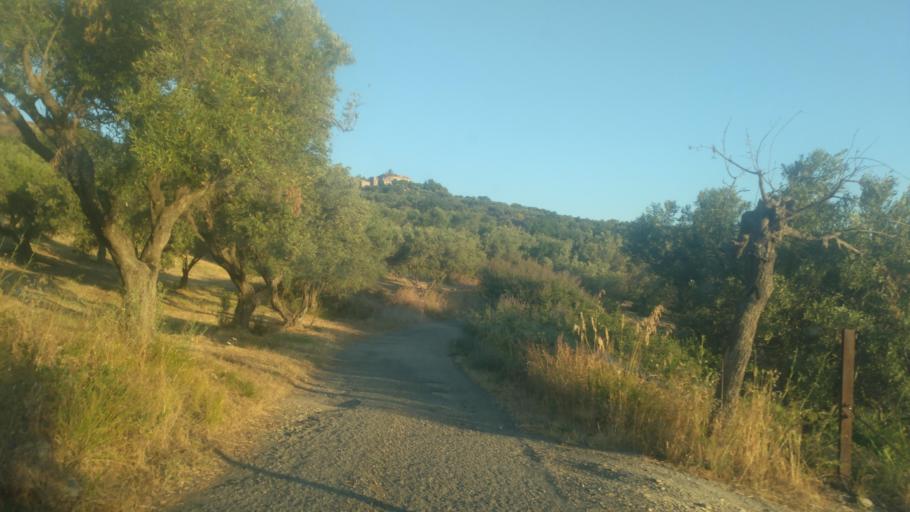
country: IT
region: Calabria
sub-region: Provincia di Catanzaro
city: Staletti
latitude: 38.7728
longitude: 16.5500
